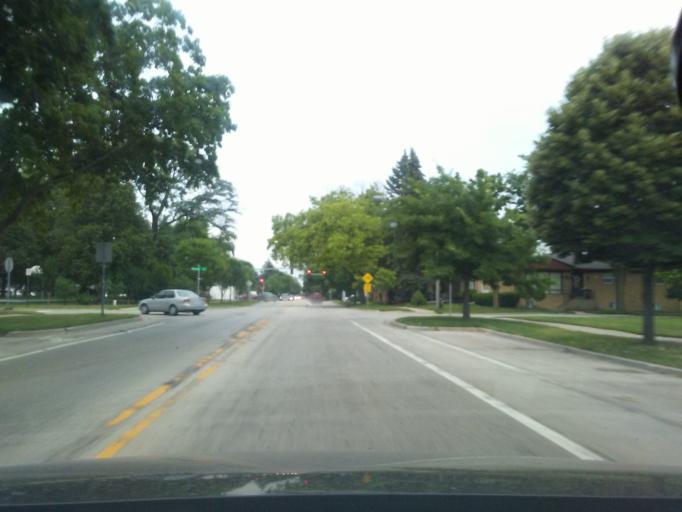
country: US
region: Illinois
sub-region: Cook County
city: Skokie
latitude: 42.0190
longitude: -87.7397
